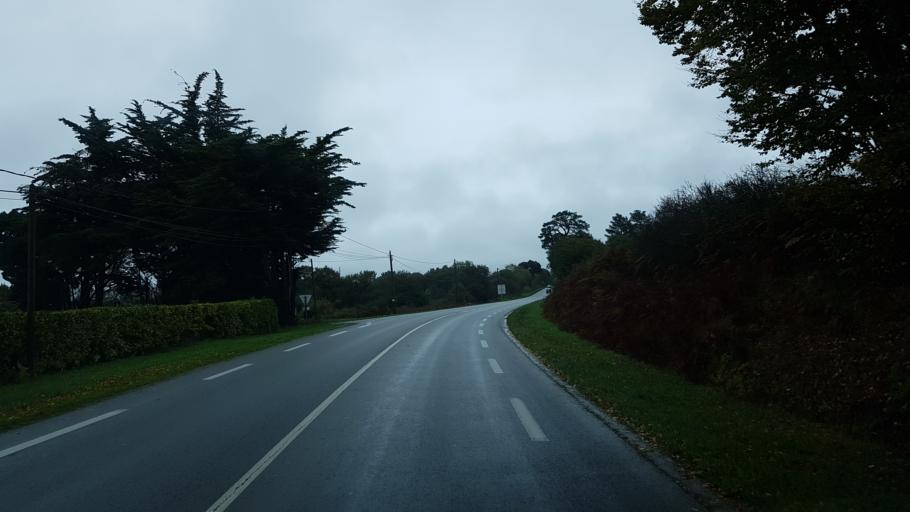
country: FR
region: Brittany
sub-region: Departement du Morbihan
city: Sarzeau
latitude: 47.5293
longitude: -2.8063
